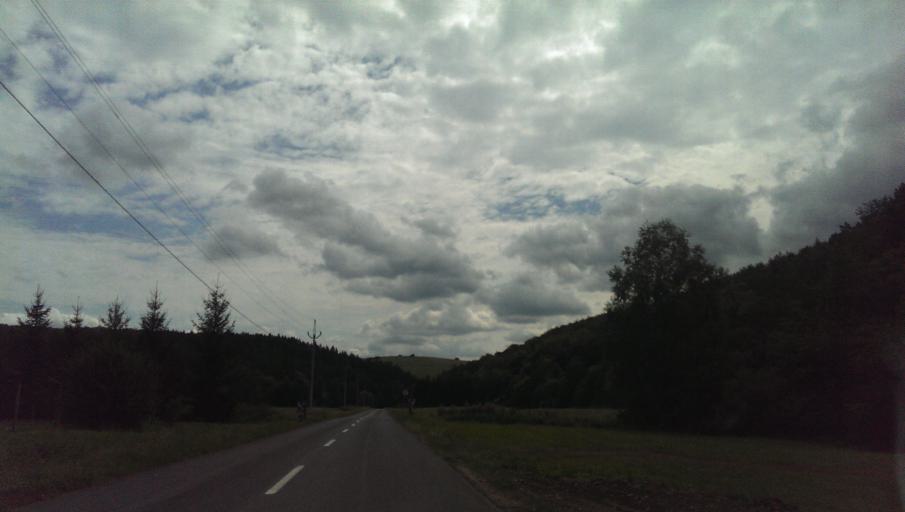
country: CZ
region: South Moravian
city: Velka nad Velickou
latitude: 48.8931
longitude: 17.5759
